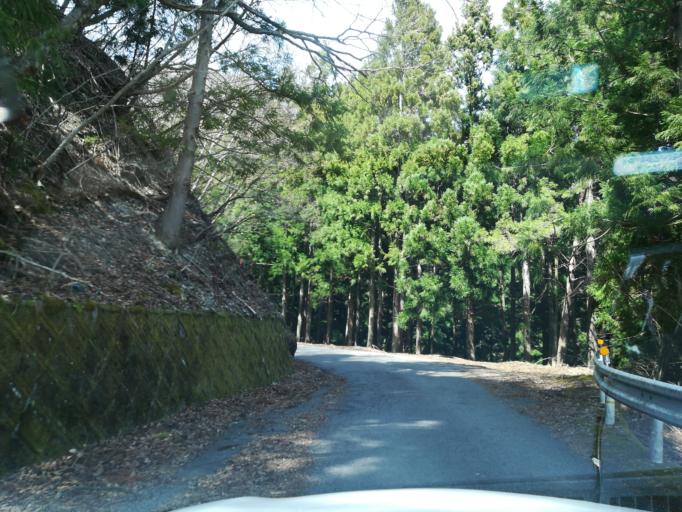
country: JP
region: Tokushima
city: Wakimachi
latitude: 33.8878
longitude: 134.0511
